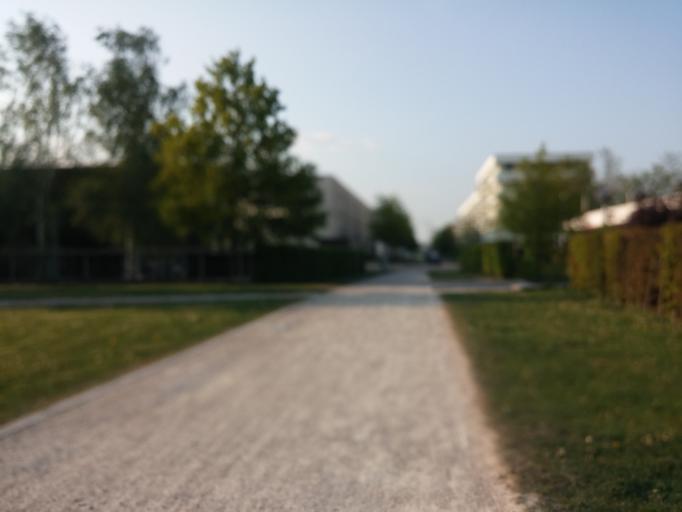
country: DE
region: Bavaria
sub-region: Upper Bavaria
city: Haar
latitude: 48.1279
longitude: 11.6890
